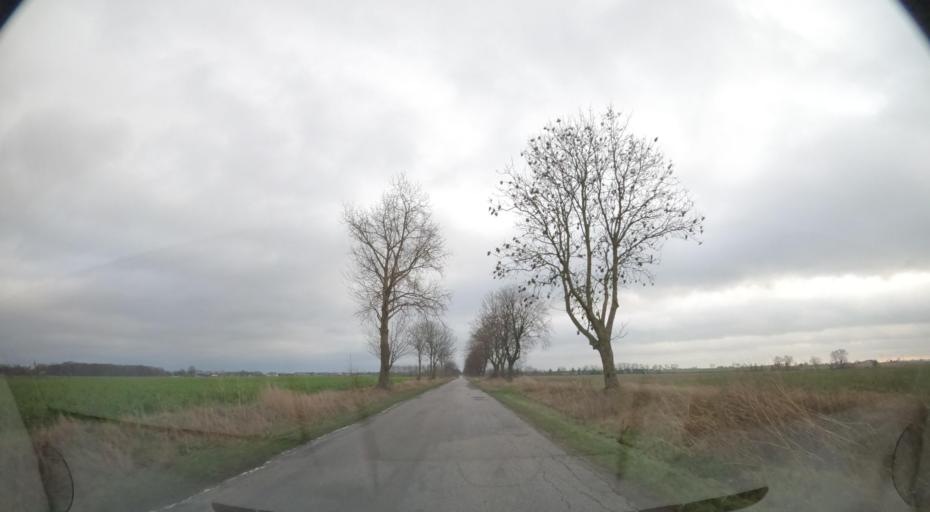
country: PL
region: Greater Poland Voivodeship
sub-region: Powiat pilski
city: Lobzenica
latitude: 53.2632
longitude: 17.2241
